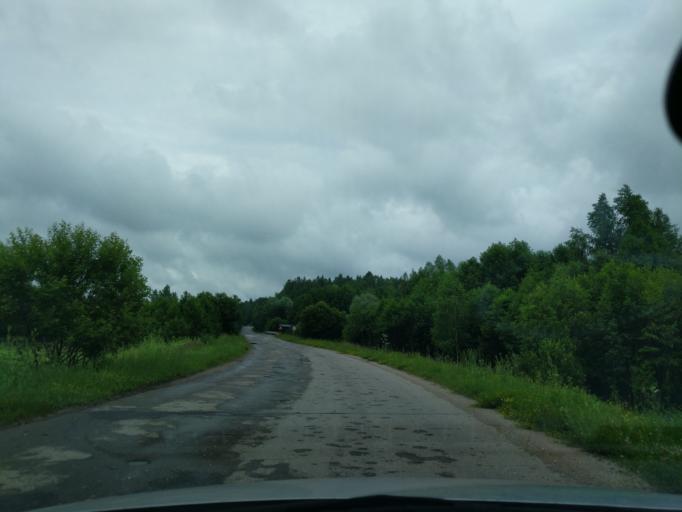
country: RU
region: Kaluga
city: Myatlevo
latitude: 54.8115
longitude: 35.6793
